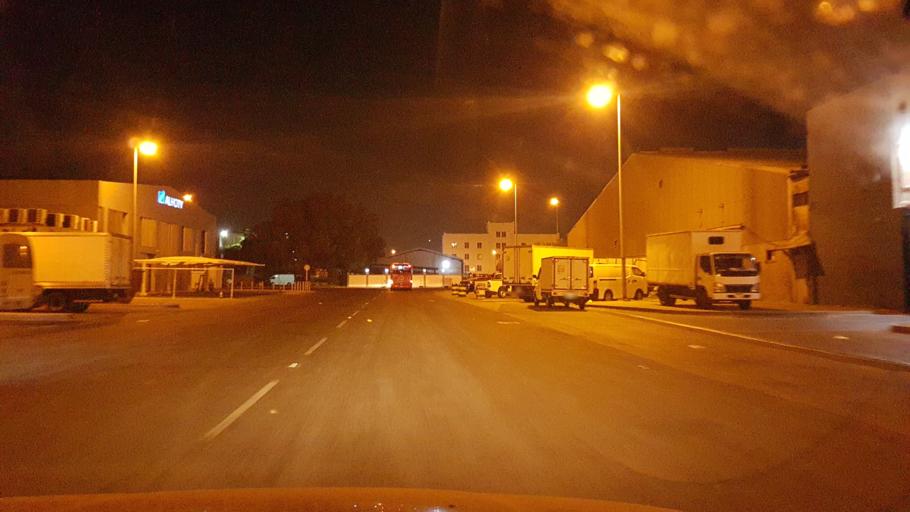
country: BH
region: Manama
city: Manama
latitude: 26.1991
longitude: 50.5968
